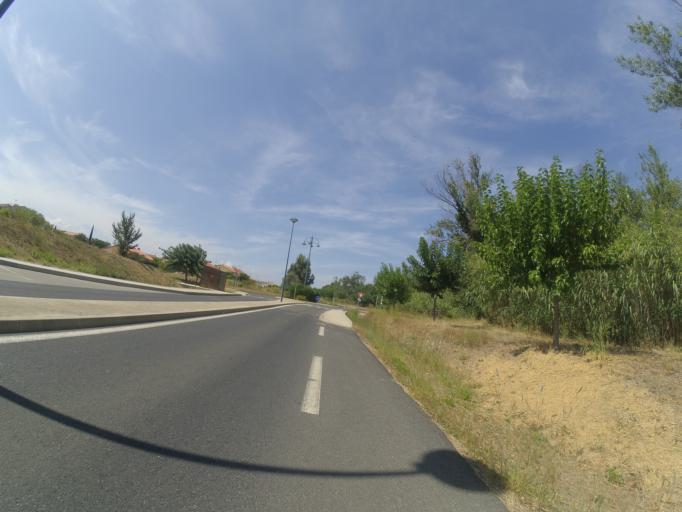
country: FR
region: Languedoc-Roussillon
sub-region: Departement des Pyrenees-Orientales
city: Peyrestortes
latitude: 42.7556
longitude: 2.8449
